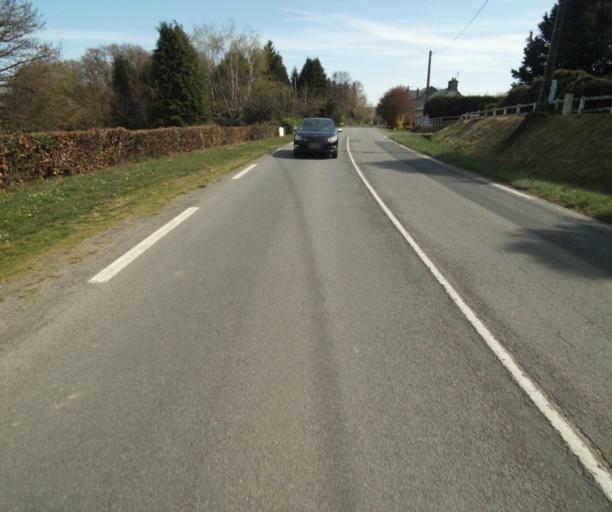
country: FR
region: Limousin
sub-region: Departement de la Correze
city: Seilhac
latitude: 45.3575
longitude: 1.7304
